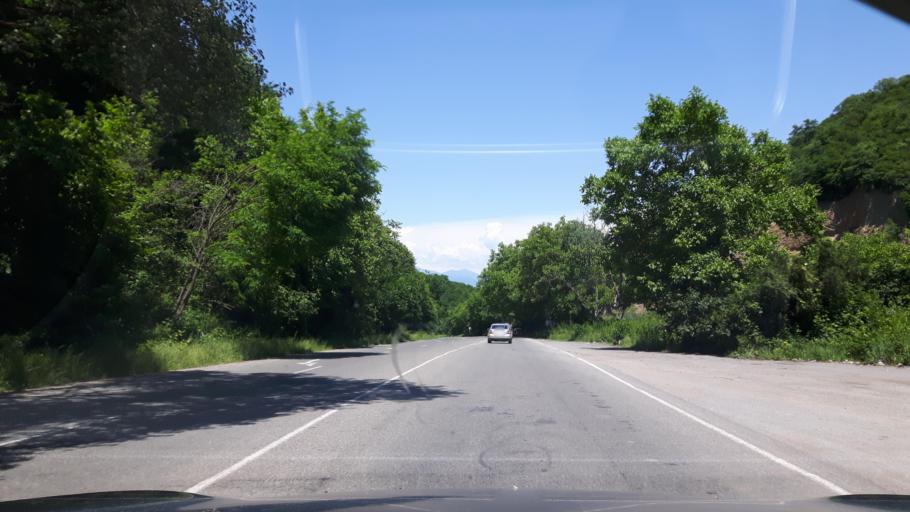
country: GE
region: Kakheti
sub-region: Gurjaani
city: Gurjaani
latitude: 41.6724
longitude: 45.8359
